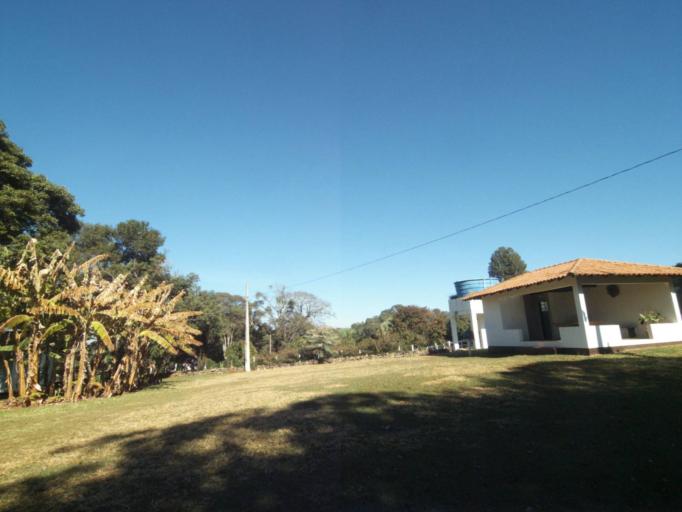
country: BR
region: Parana
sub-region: Tibagi
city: Tibagi
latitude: -24.3829
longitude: -50.3248
